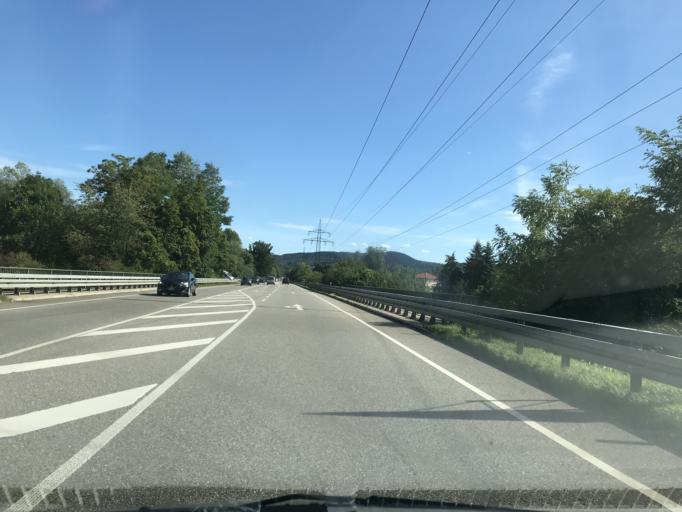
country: CH
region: Aargau
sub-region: Bezirk Rheinfelden
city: Mumpf
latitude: 47.5758
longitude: 7.9139
